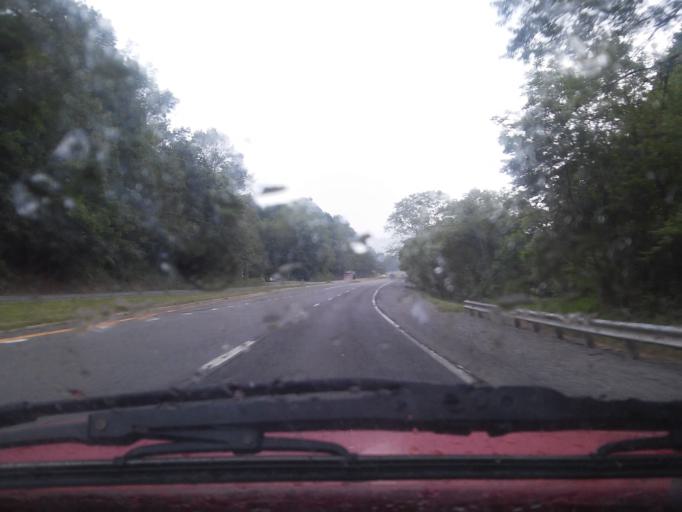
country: US
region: Virginia
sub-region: Montgomery County
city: Prices Fork
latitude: 37.3045
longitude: -80.5084
